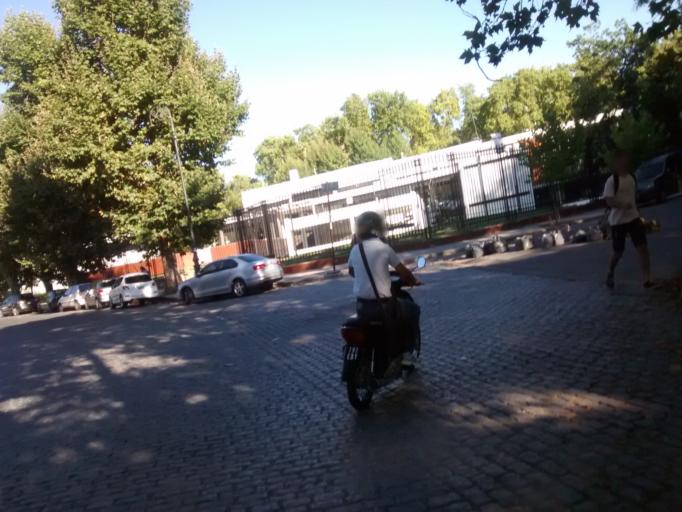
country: AR
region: Buenos Aires
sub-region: Partido de La Plata
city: La Plata
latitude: -34.9094
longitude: -57.9418
